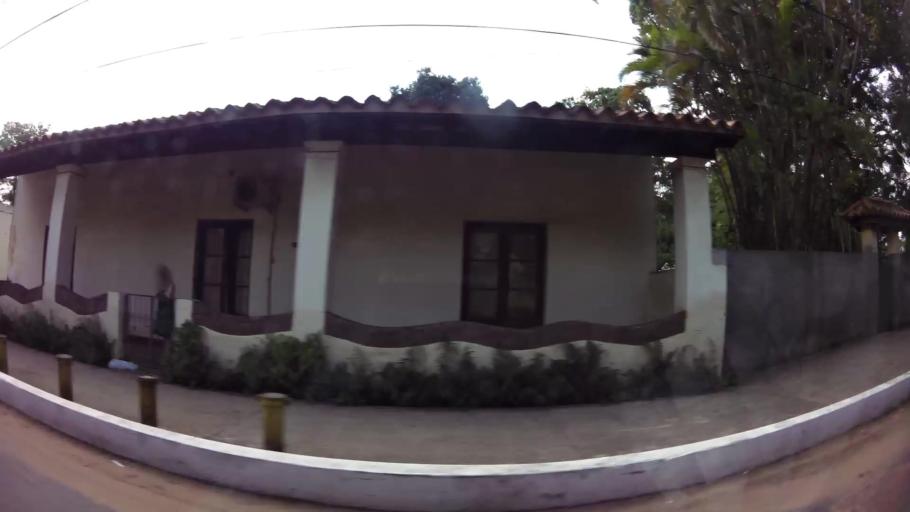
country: PY
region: Central
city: San Lorenzo
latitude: -25.3404
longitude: -57.5098
